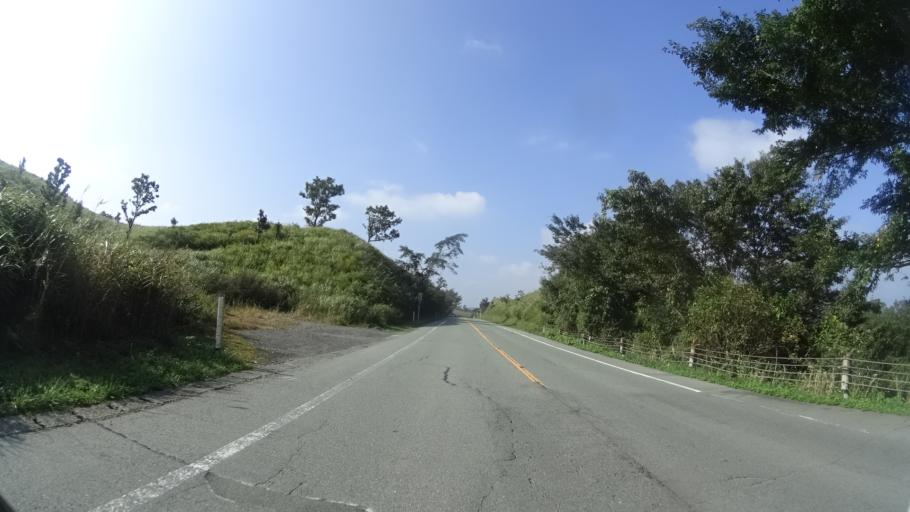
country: JP
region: Kumamoto
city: Aso
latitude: 33.0259
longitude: 131.0663
